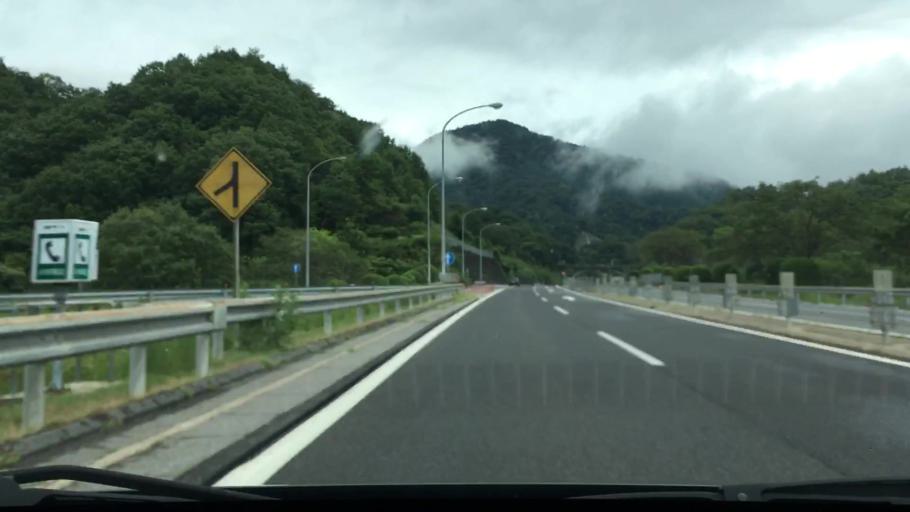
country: JP
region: Hiroshima
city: Hiroshima-shi
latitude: 34.5511
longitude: 132.4519
